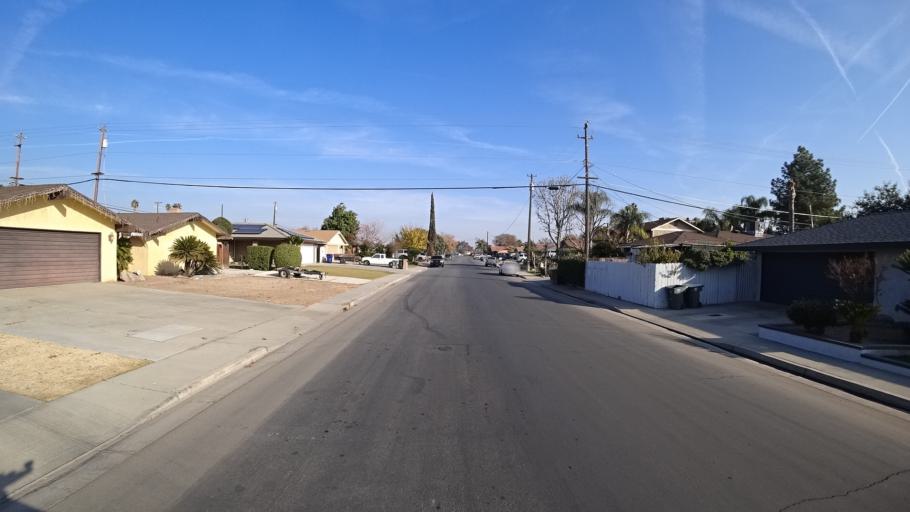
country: US
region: California
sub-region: Kern County
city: Bakersfield
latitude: 35.3235
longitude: -119.0281
